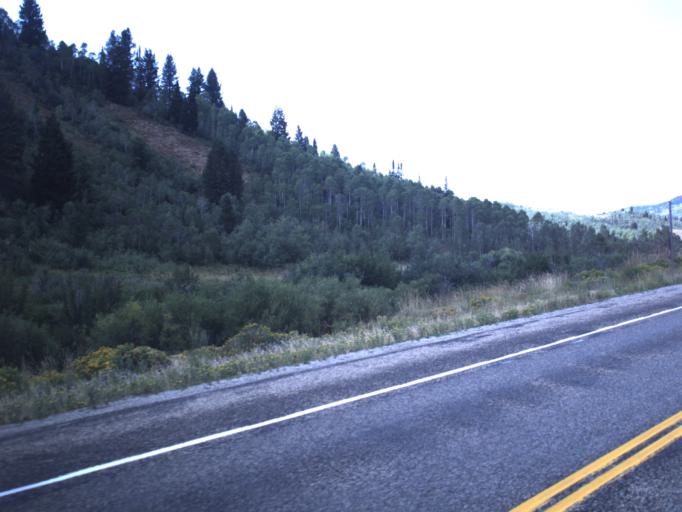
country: US
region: Utah
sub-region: Cache County
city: Richmond
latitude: 41.9000
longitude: -111.5637
